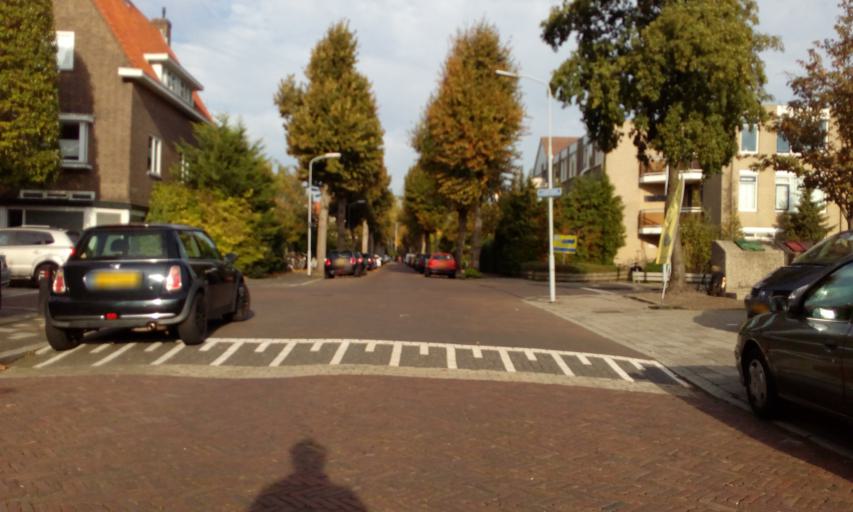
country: NL
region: South Holland
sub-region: Gemeente Leidschendam-Voorburg
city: Voorburg
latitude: 52.0824
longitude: 4.3874
